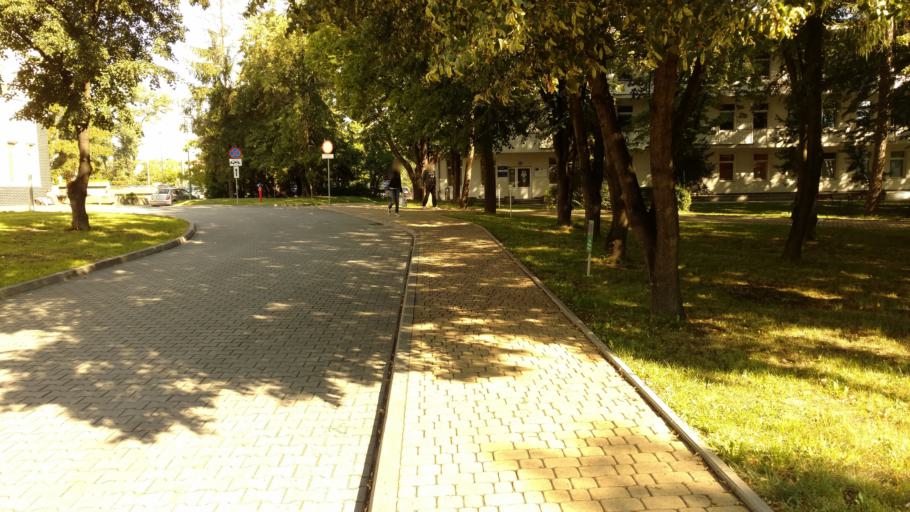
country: PL
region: Lesser Poland Voivodeship
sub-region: Krakow
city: Krakow
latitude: 50.0904
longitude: 19.9345
